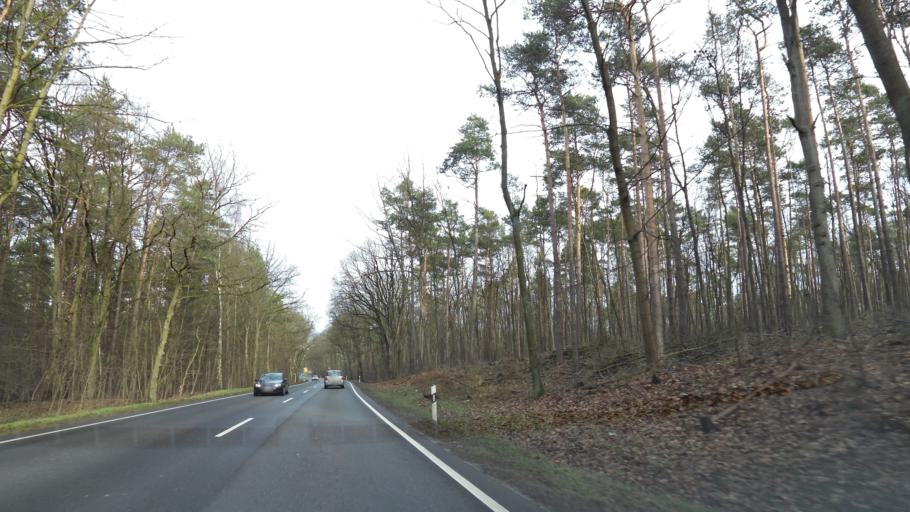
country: DE
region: Brandenburg
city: Strausberg
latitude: 52.5542
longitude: 13.8541
